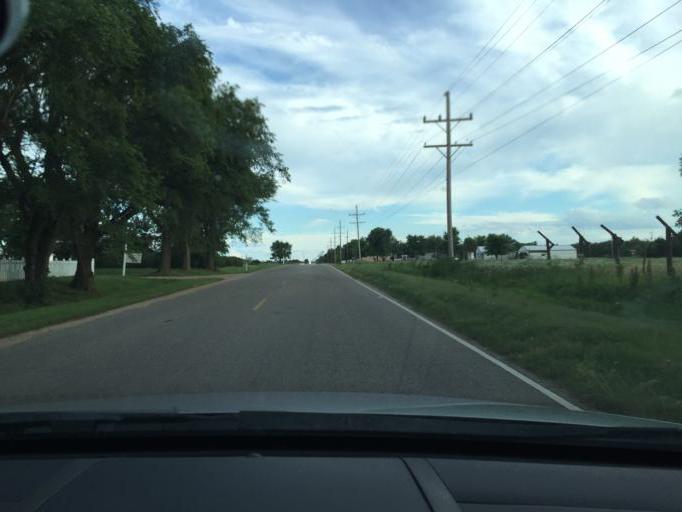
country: US
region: Kansas
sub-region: Reno County
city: Haven
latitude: 37.9324
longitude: -97.8852
